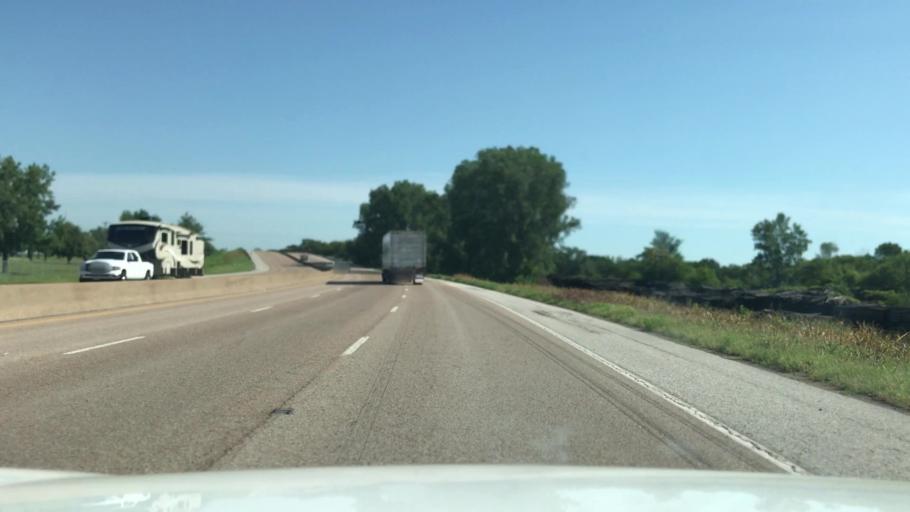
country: US
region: Illinois
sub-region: Madison County
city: Madison
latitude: 38.6937
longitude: -90.1679
